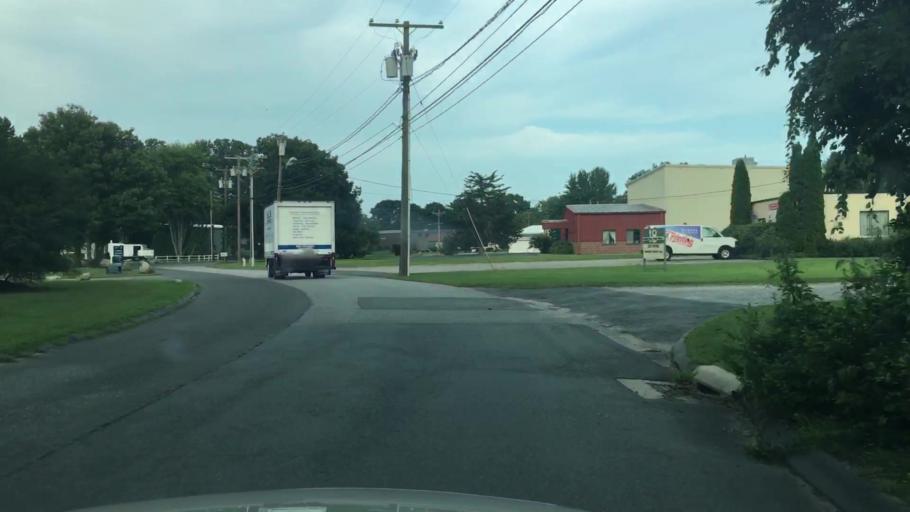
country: US
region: Connecticut
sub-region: Middlesex County
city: Essex Village
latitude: 41.3477
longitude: -72.4133
